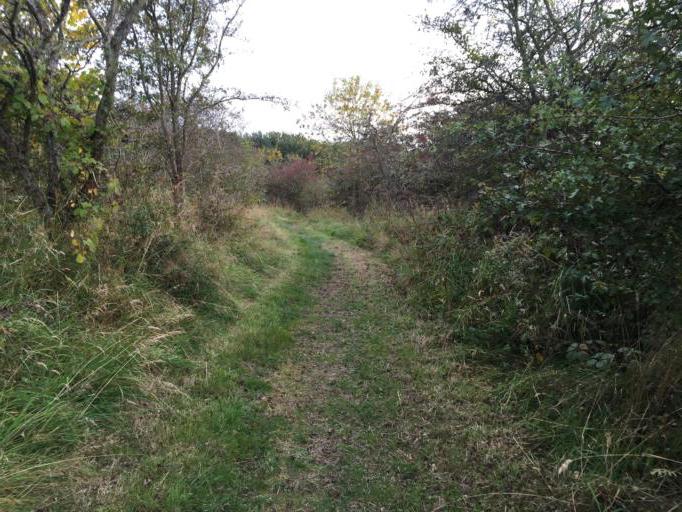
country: GB
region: Scotland
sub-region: West Lothian
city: Livingston
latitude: 55.9329
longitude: -3.5128
